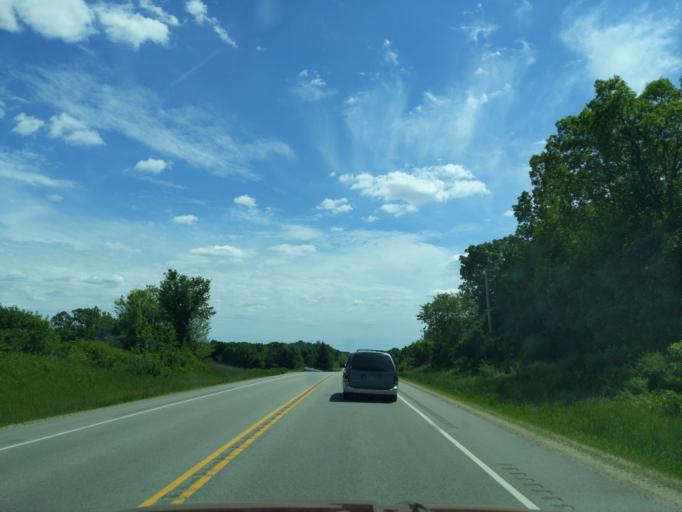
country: US
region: Wisconsin
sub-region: Columbia County
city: Poynette
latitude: 43.4234
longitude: -89.3281
